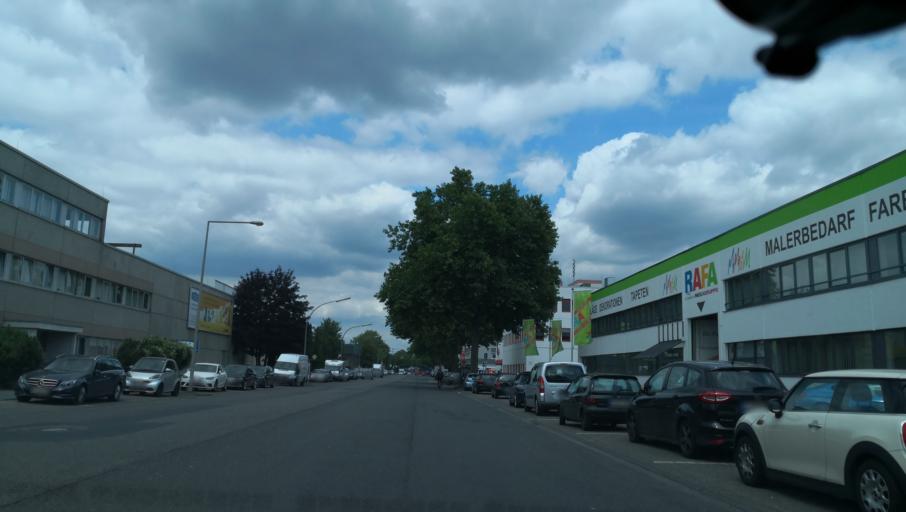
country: DE
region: North Rhine-Westphalia
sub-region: Regierungsbezirk Koln
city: Mengenich
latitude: 50.9734
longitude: 6.8910
